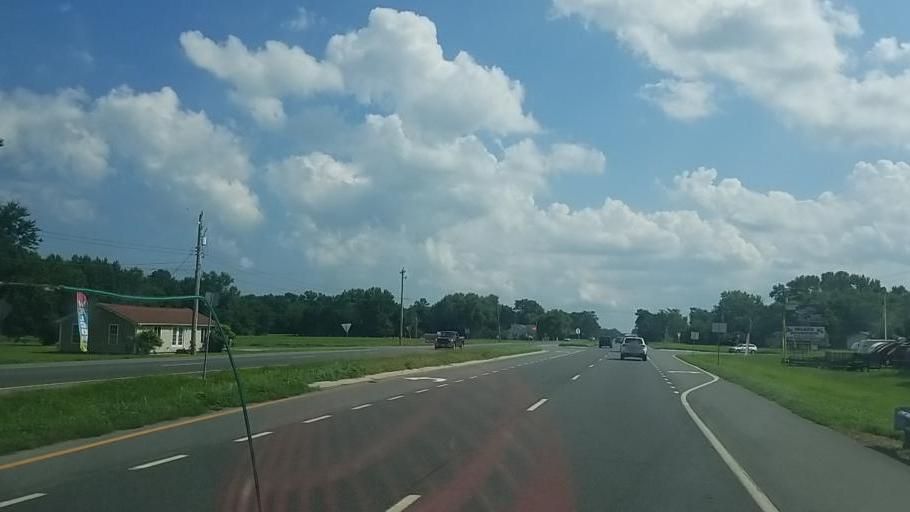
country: US
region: Delaware
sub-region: Sussex County
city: Selbyville
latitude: 38.5020
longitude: -75.2375
